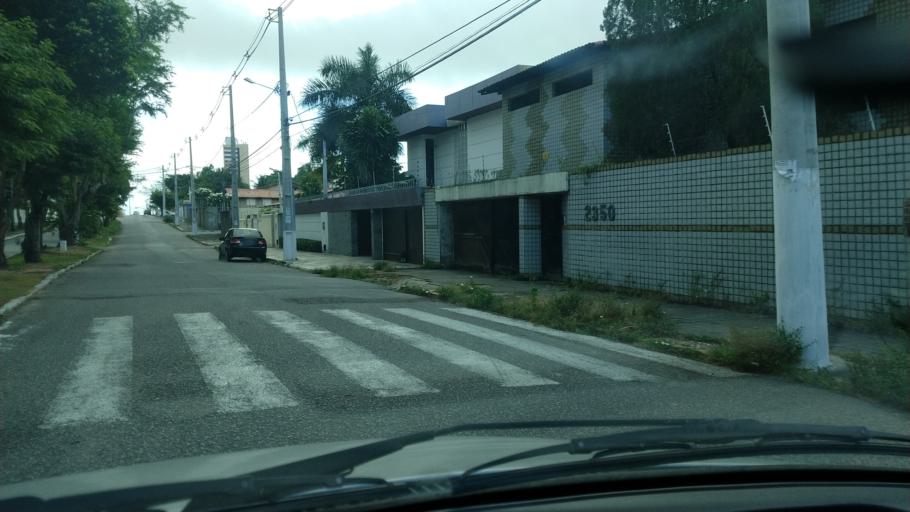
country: BR
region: Rio Grande do Norte
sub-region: Natal
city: Natal
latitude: -5.8162
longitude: -35.2205
